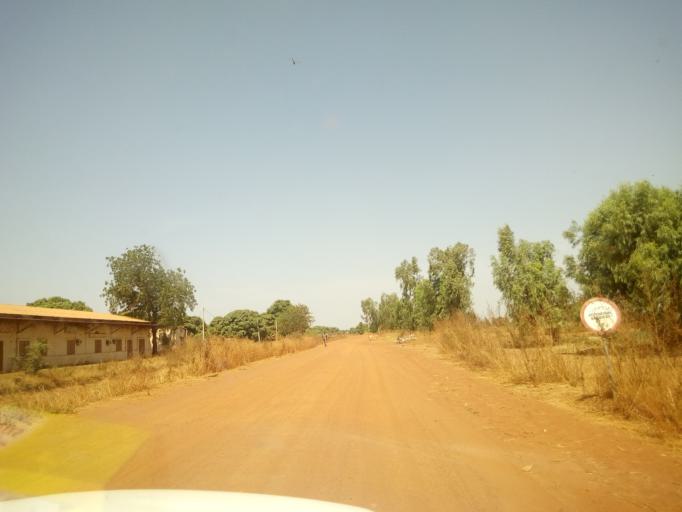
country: ML
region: Bamako
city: Bamako
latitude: 12.6225
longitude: -7.7786
